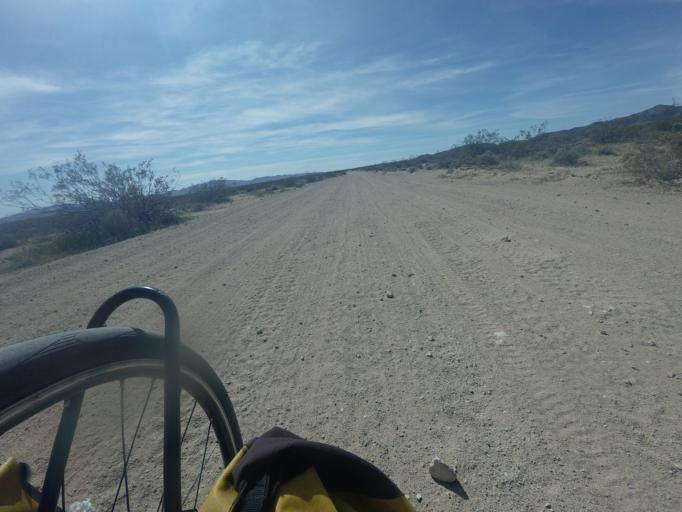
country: US
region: California
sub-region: San Bernardino County
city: Searles Valley
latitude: 35.5755
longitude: -117.4334
